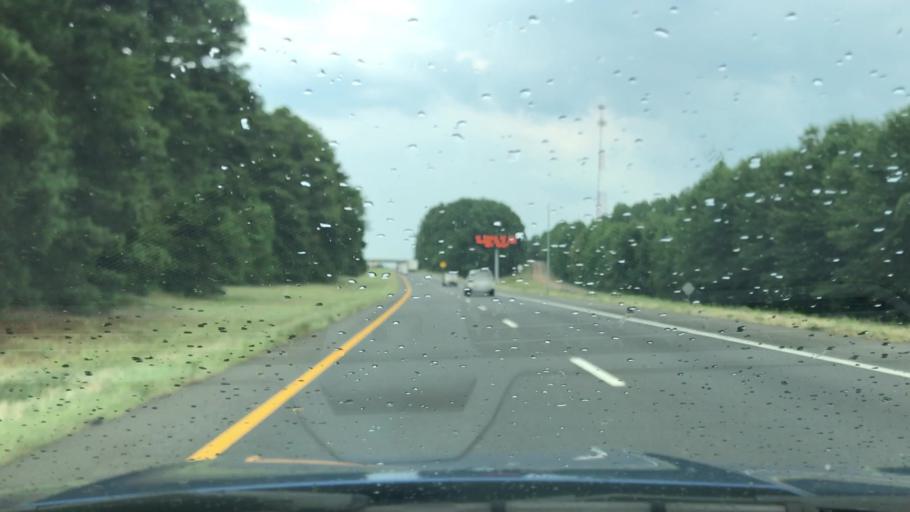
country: US
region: Texas
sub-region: Harrison County
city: Marshall
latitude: 32.4875
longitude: -94.4358
